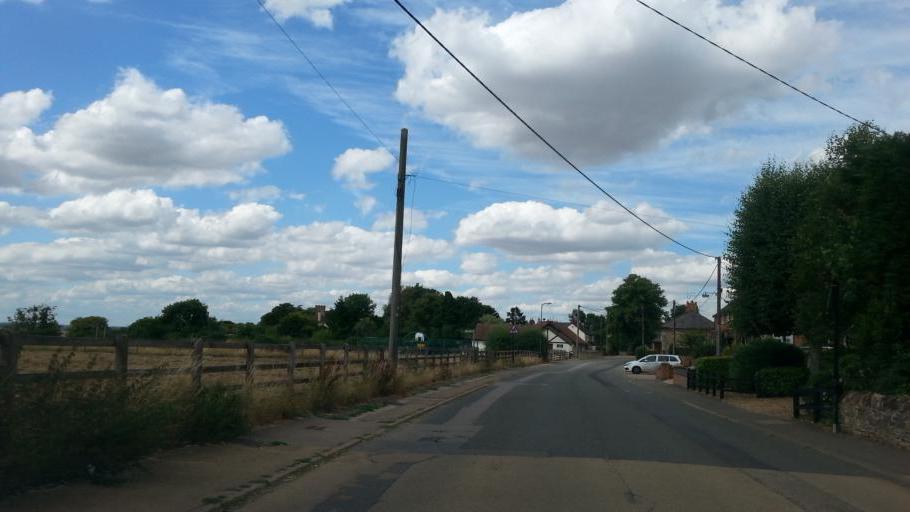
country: GB
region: England
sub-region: Northamptonshire
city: Silverstone
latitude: 52.0885
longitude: -0.9923
